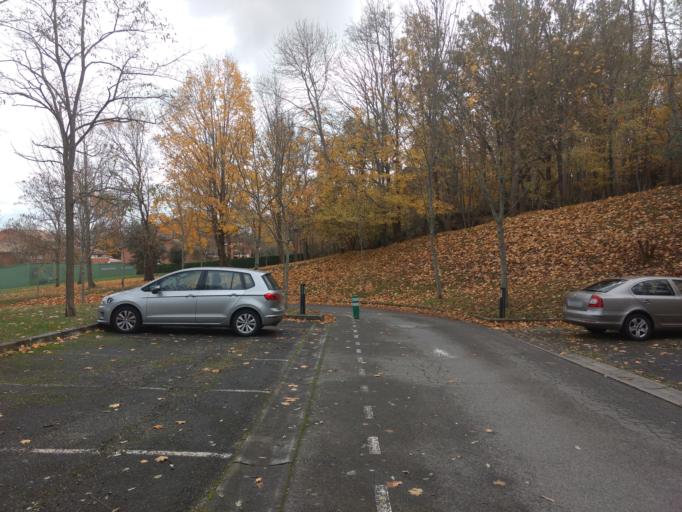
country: FR
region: Midi-Pyrenees
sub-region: Departement de la Haute-Garonne
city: Ramonville-Saint-Agne
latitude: 43.5563
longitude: 1.4620
